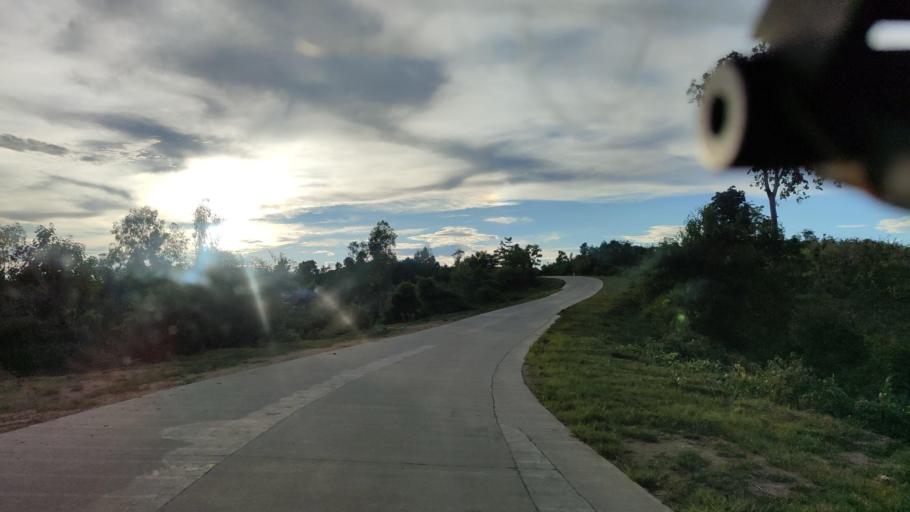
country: MM
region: Magway
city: Taungdwingyi
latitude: 20.0391
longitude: 95.7831
